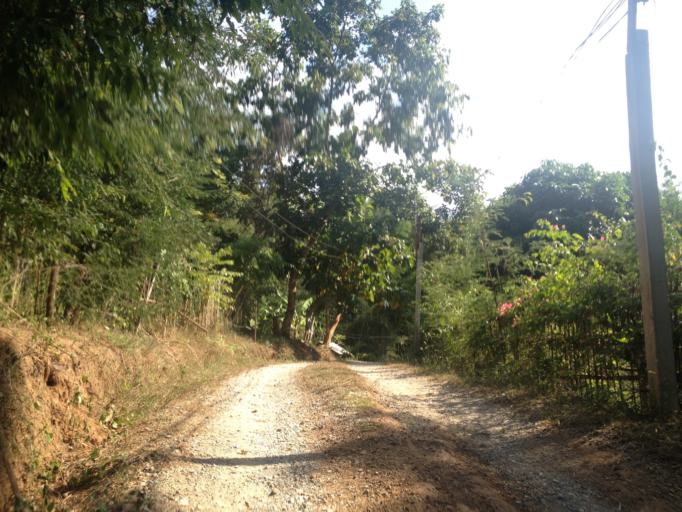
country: TH
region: Chiang Mai
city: Hang Dong
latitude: 18.7368
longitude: 98.9071
